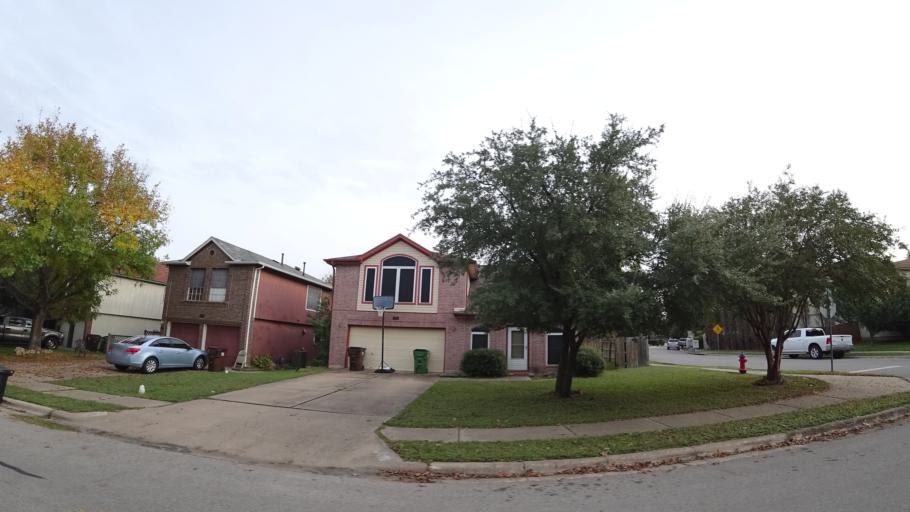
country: US
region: Texas
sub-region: Williamson County
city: Round Rock
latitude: 30.5068
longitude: -97.6625
